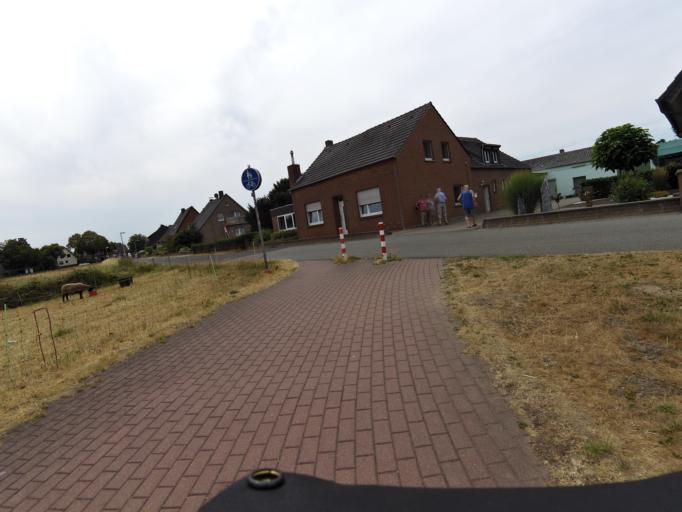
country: DE
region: North Rhine-Westphalia
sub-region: Regierungsbezirk Dusseldorf
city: Kevelaer
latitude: 51.5698
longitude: 6.2510
